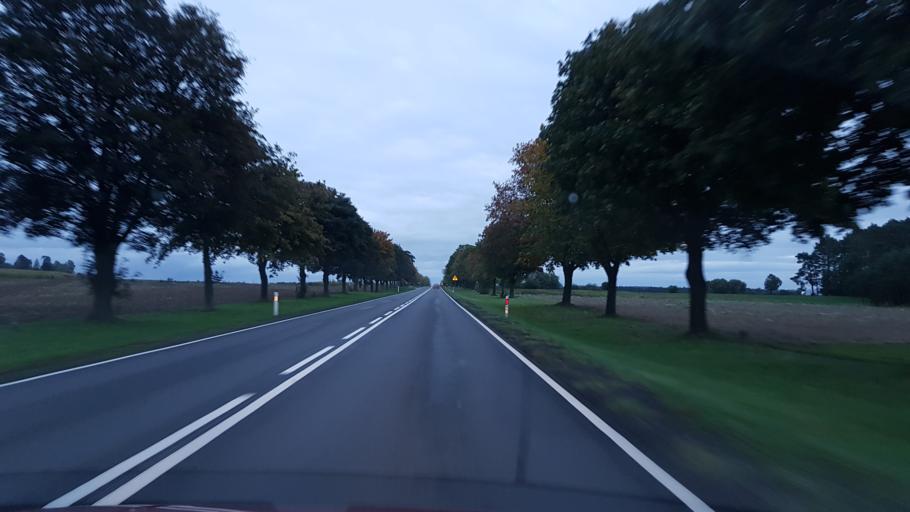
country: PL
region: West Pomeranian Voivodeship
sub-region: Powiat choszczenski
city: Recz
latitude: 53.2705
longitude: 15.4911
